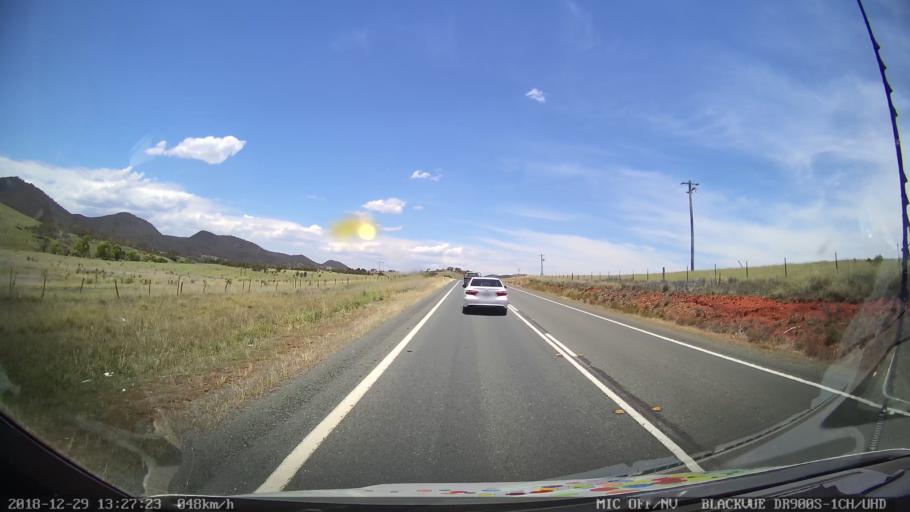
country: AU
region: New South Wales
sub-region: Cooma-Monaro
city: Cooma
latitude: -35.8657
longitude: 149.1594
